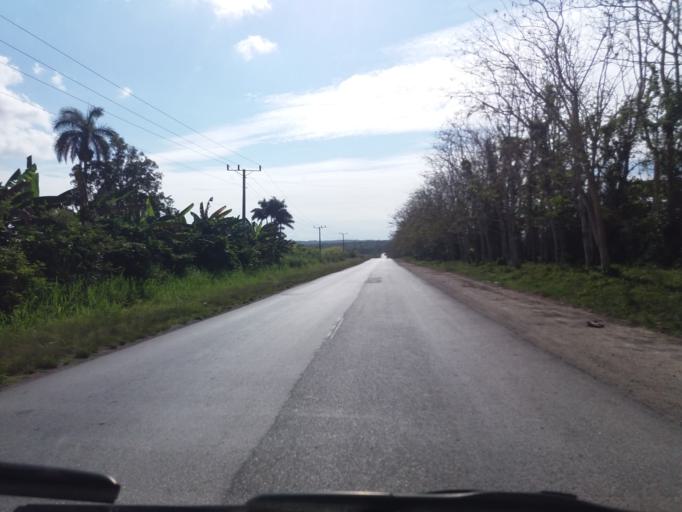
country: CU
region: Cienfuegos
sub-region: Municipio de Cienfuegos
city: Cienfuegos
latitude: 22.1656
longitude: -80.3820
